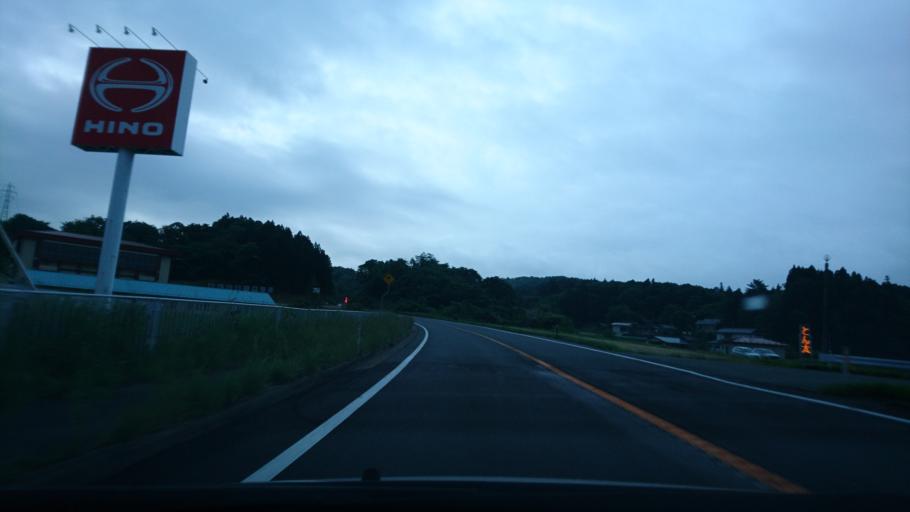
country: JP
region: Iwate
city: Ichinoseki
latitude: 38.9148
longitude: 141.1078
